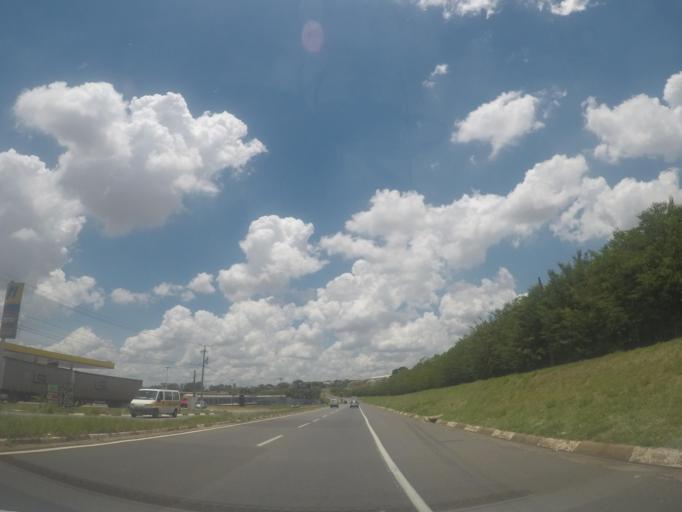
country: BR
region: Sao Paulo
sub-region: Hortolandia
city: Hortolandia
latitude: -22.8259
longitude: -47.2001
